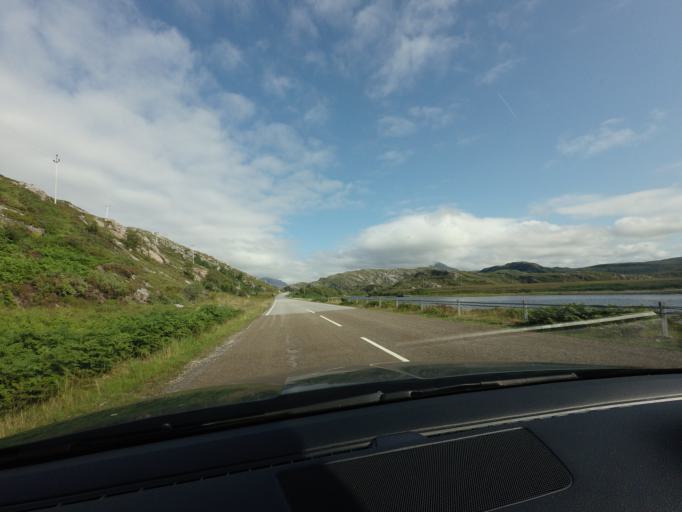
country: GB
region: Scotland
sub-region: Highland
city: Ullapool
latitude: 58.3797
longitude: -5.0289
